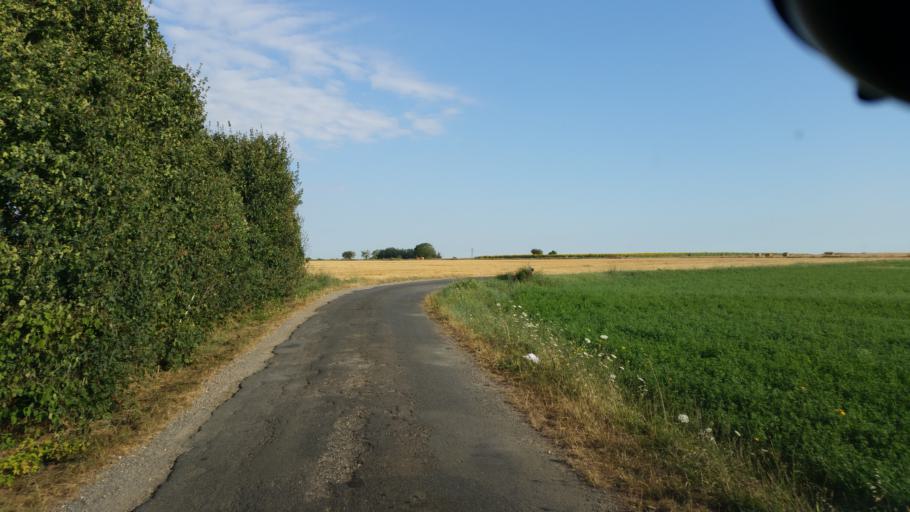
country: FR
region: Poitou-Charentes
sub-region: Departement de la Charente-Maritime
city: Saint-Jean-de-Liversay
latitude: 46.2319
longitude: -0.8899
